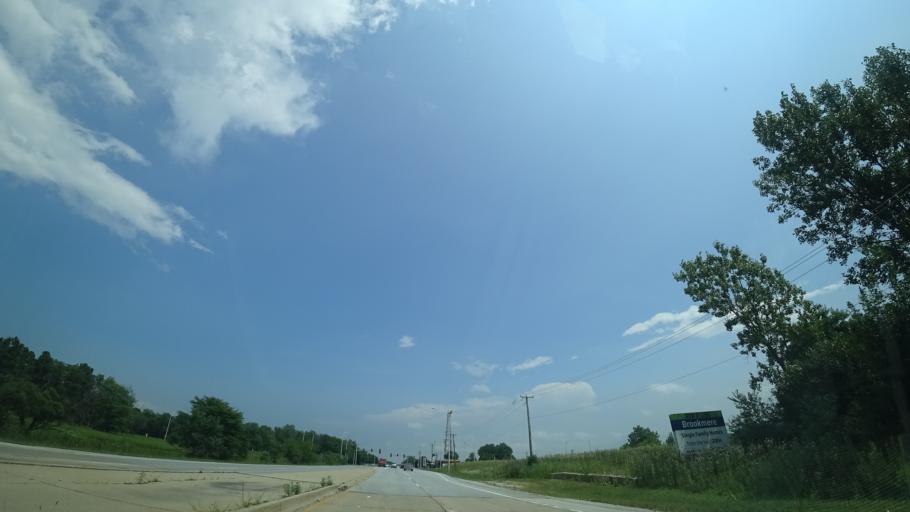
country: US
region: Illinois
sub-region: Cook County
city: Matteson
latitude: 41.5280
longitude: -87.7352
